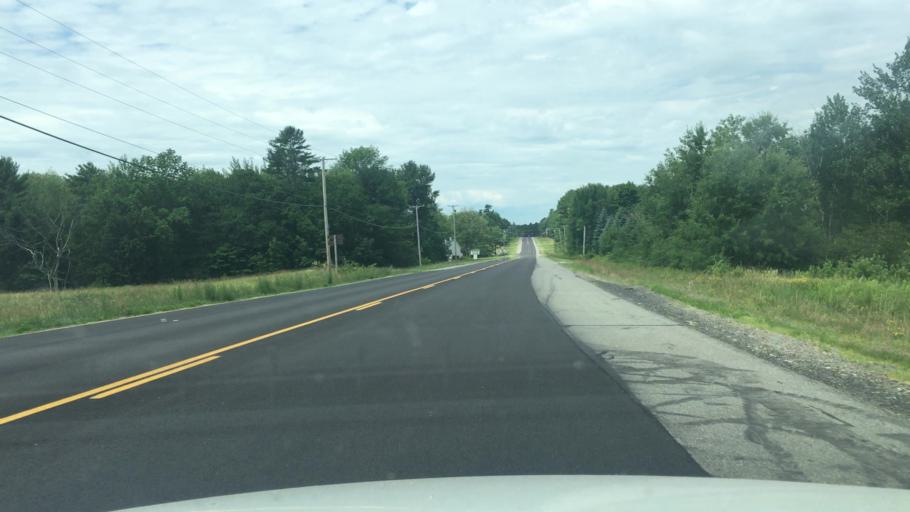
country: US
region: Maine
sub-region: Waldo County
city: Palermo
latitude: 44.3772
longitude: -69.4490
